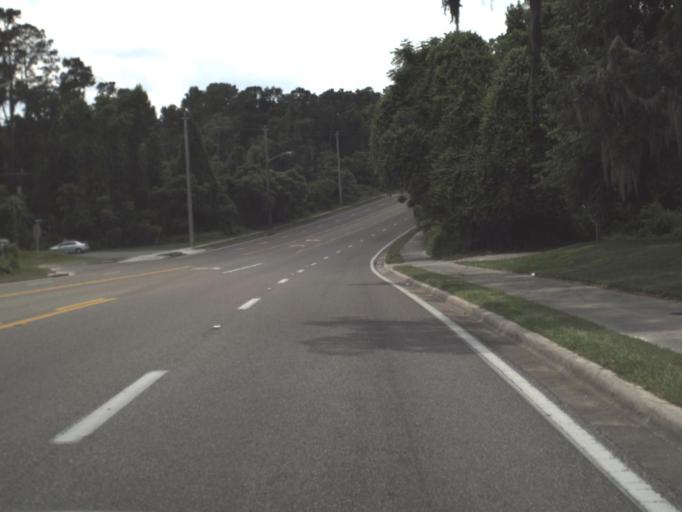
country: US
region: Florida
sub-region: Columbia County
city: Watertown
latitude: 30.1830
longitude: -82.6128
